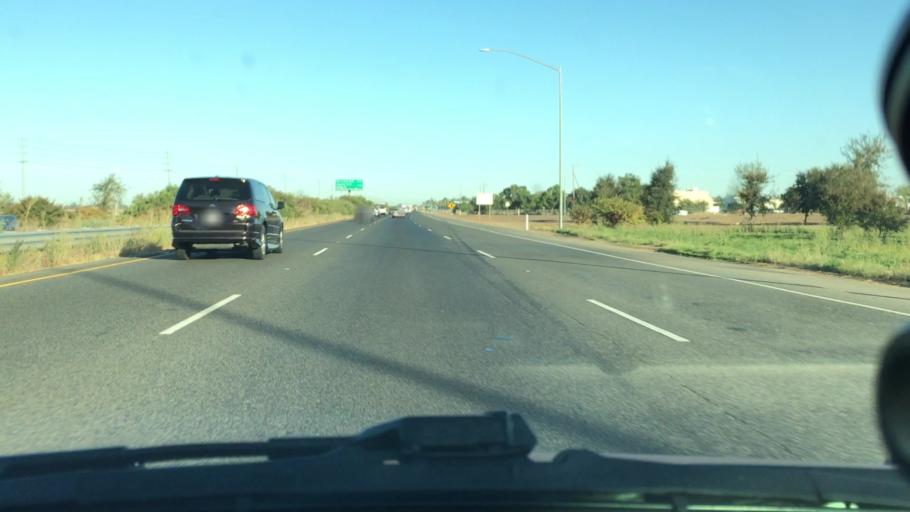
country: US
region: California
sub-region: Sacramento County
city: Elk Grove
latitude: 38.3769
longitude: -121.3624
